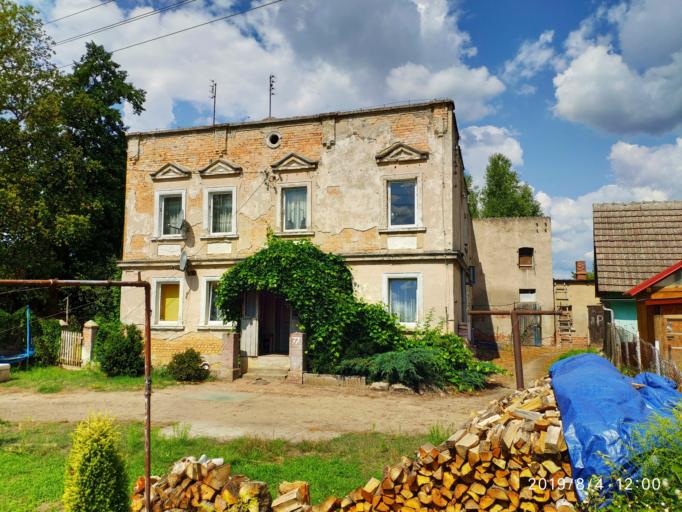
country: PL
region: Lubusz
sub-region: Powiat nowosolski
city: Kozuchow
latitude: 51.7966
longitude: 15.5680
